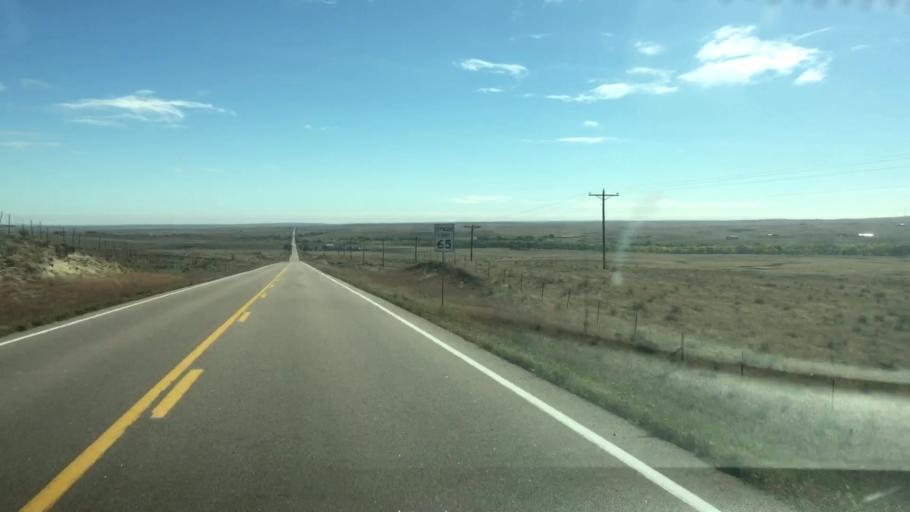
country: US
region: Colorado
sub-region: Elbert County
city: Kiowa
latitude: 39.2735
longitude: -104.1769
